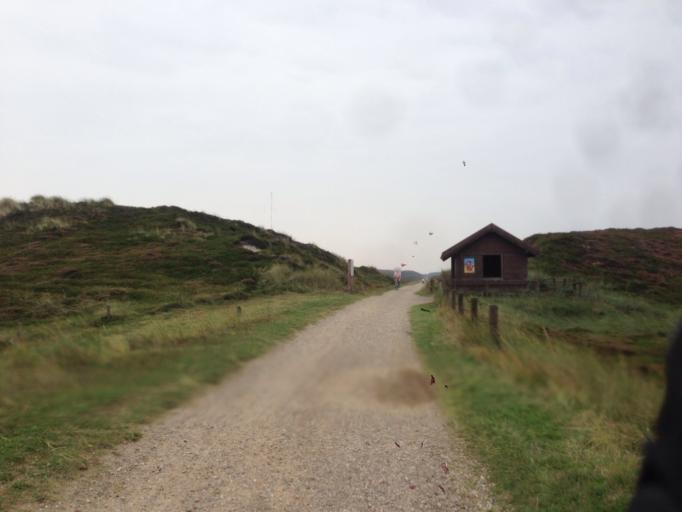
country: DE
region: Schleswig-Holstein
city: Westerland
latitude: 54.8213
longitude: 8.2942
